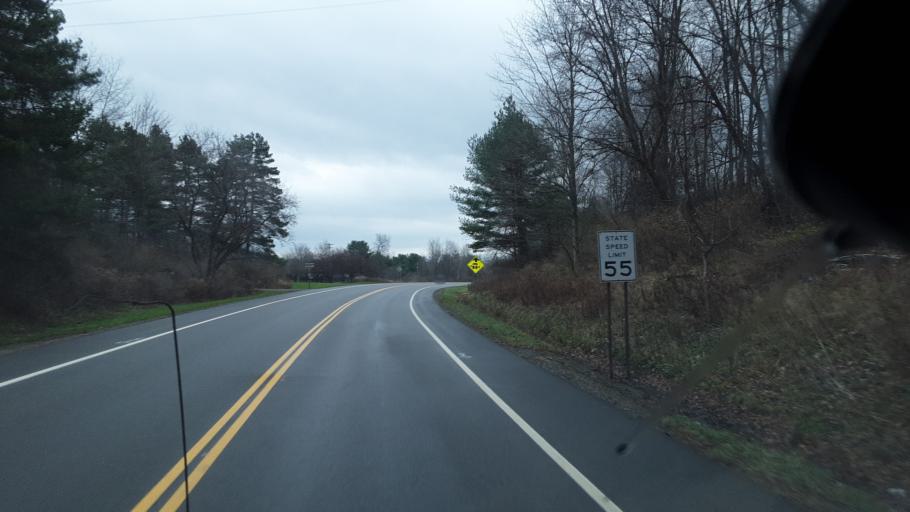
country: US
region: New York
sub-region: Allegany County
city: Houghton
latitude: 42.3633
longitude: -78.1323
